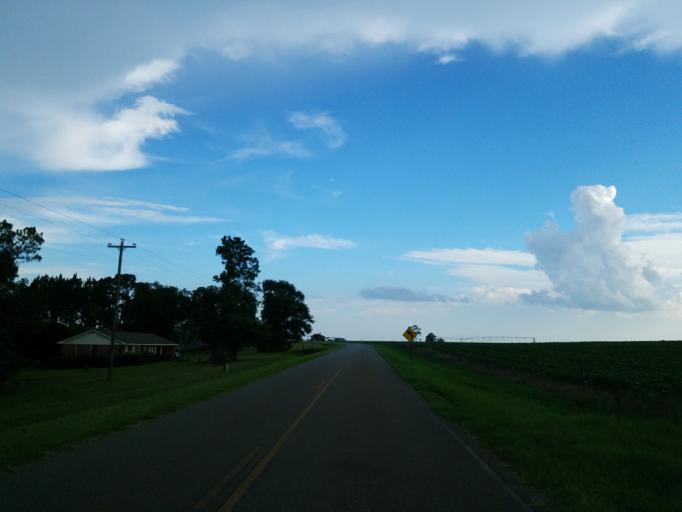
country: US
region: Georgia
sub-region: Tift County
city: Omega
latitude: 31.2700
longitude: -83.5188
